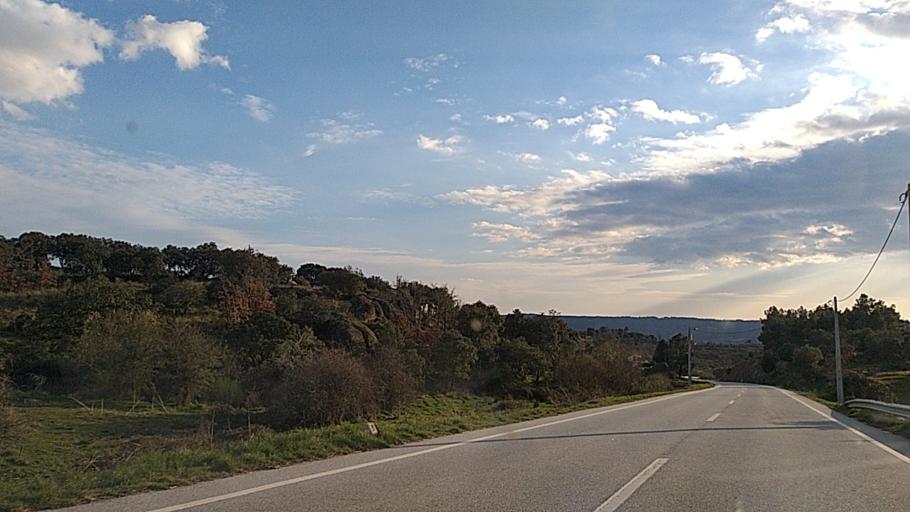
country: ES
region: Castille and Leon
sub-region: Provincia de Salamanca
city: Aldea del Obispo
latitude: 40.7102
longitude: -6.9156
